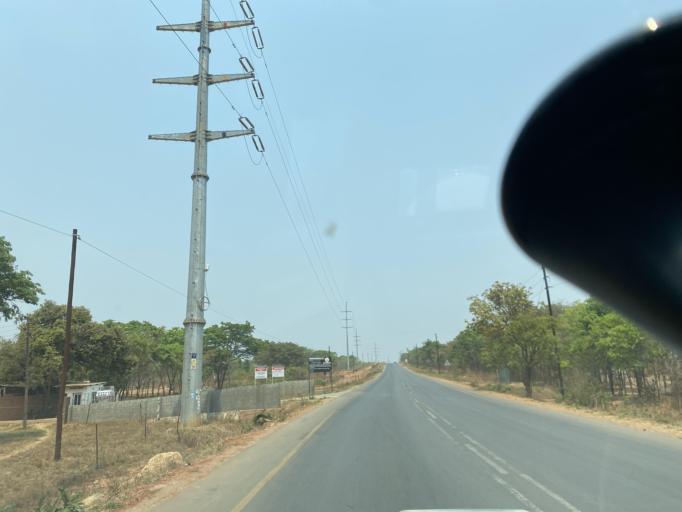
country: ZM
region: Lusaka
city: Lusaka
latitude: -15.5283
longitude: 28.4645
